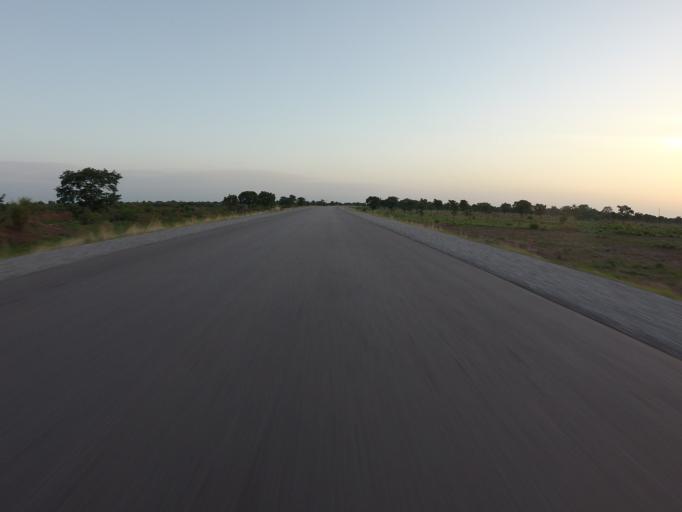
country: GH
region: Northern
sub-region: Yendi
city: Yendi
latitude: 9.9501
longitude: -0.1563
